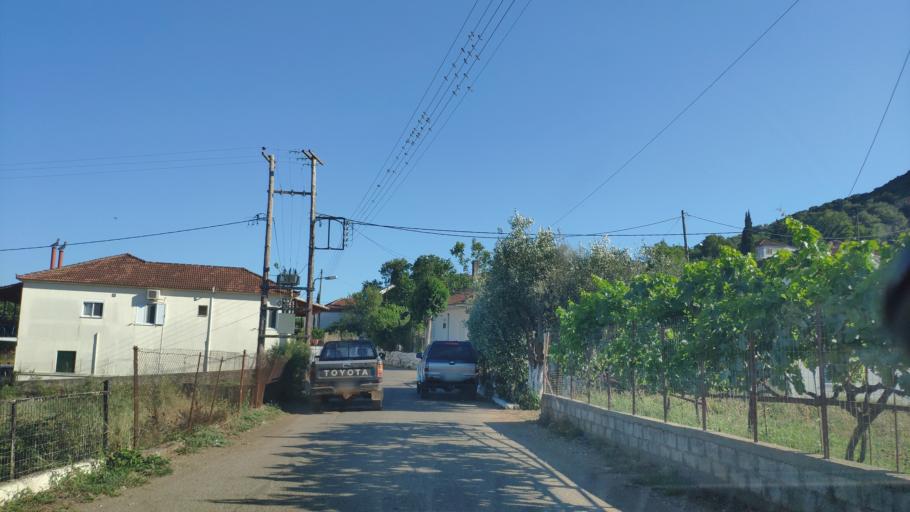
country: GR
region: West Greece
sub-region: Nomos Aitolias kai Akarnanias
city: Fitiai
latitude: 38.6616
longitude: 21.1459
